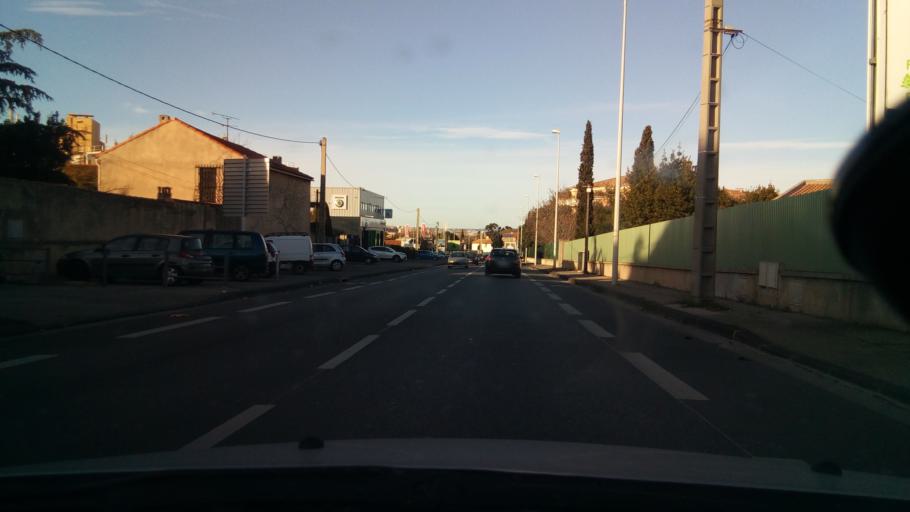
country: FR
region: Provence-Alpes-Cote d'Azur
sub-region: Departement des Bouches-du-Rhone
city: Marseille 09
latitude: 43.2424
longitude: 5.3970
